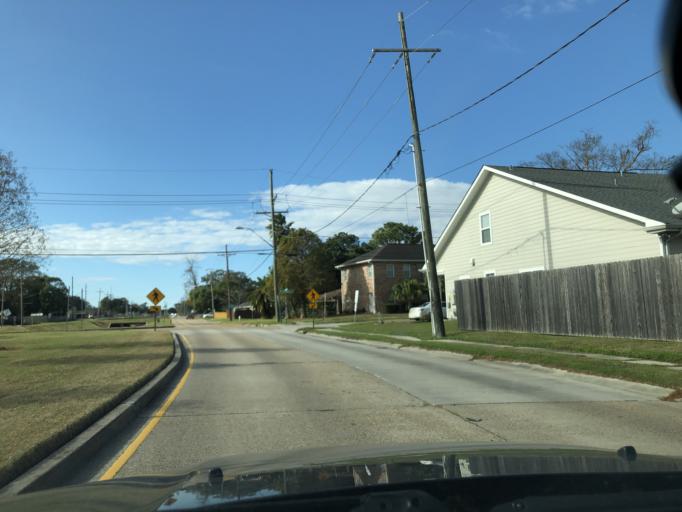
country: US
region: Louisiana
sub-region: Jefferson Parish
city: Metairie Terrace
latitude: 29.9820
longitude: -90.1669
